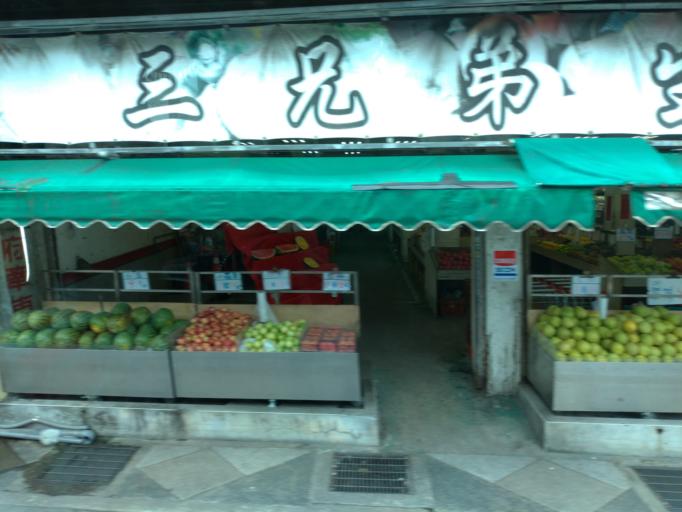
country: TW
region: Taiwan
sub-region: Keelung
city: Keelung
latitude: 25.0983
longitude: 121.7482
